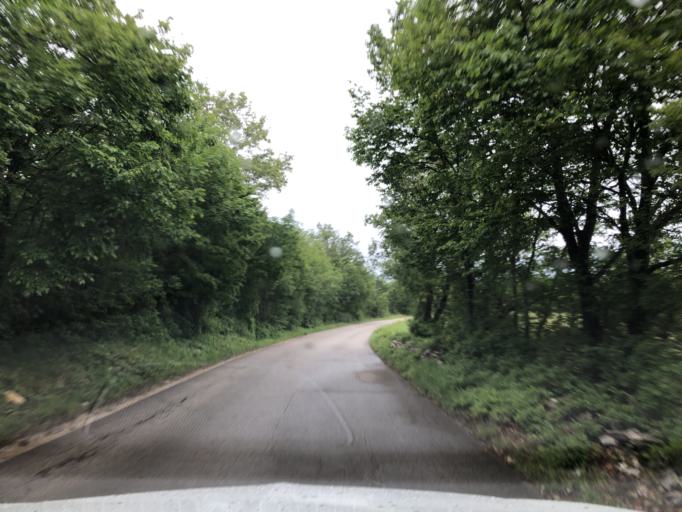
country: HR
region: Istarska
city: Buje
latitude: 45.4345
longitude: 13.6786
